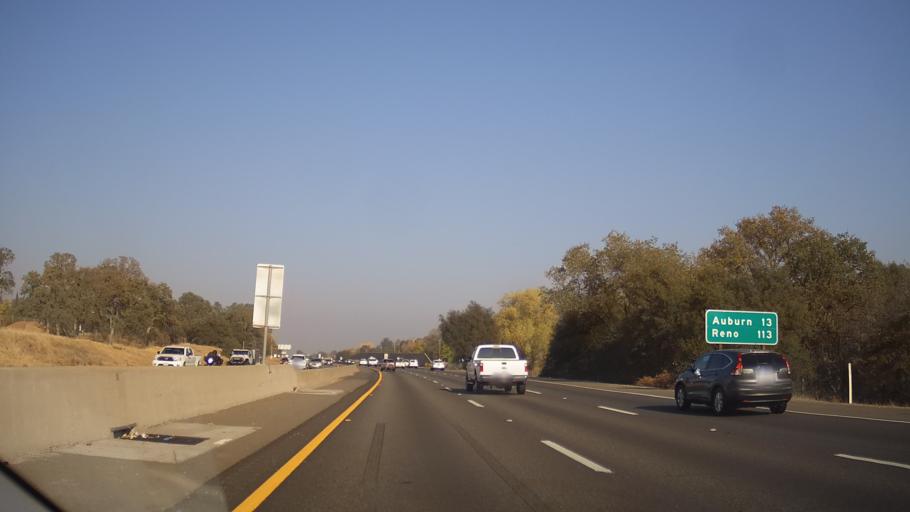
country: US
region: California
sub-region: Placer County
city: Rocklin
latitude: 38.7784
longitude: -121.2350
